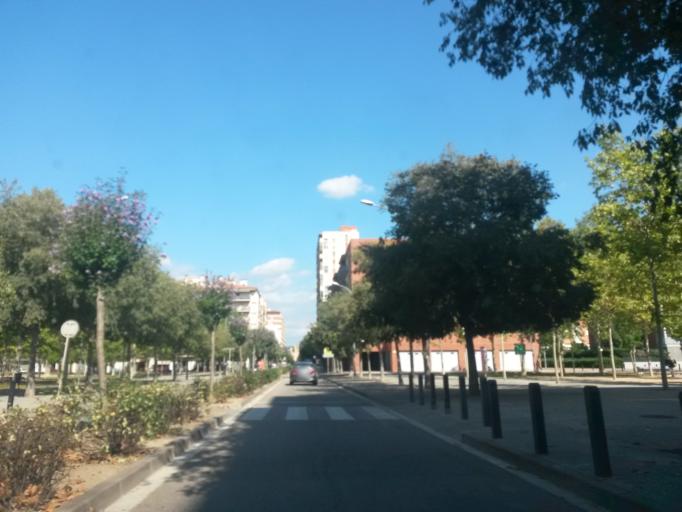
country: ES
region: Catalonia
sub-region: Provincia de Girona
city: Salt
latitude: 41.9708
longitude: 2.7925
